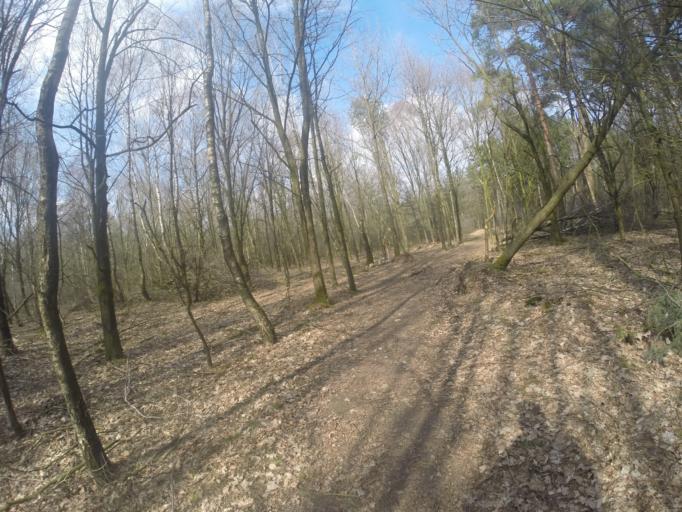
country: NL
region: Gelderland
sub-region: Gemeente Lochem
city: Almen
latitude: 52.1474
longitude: 6.3240
